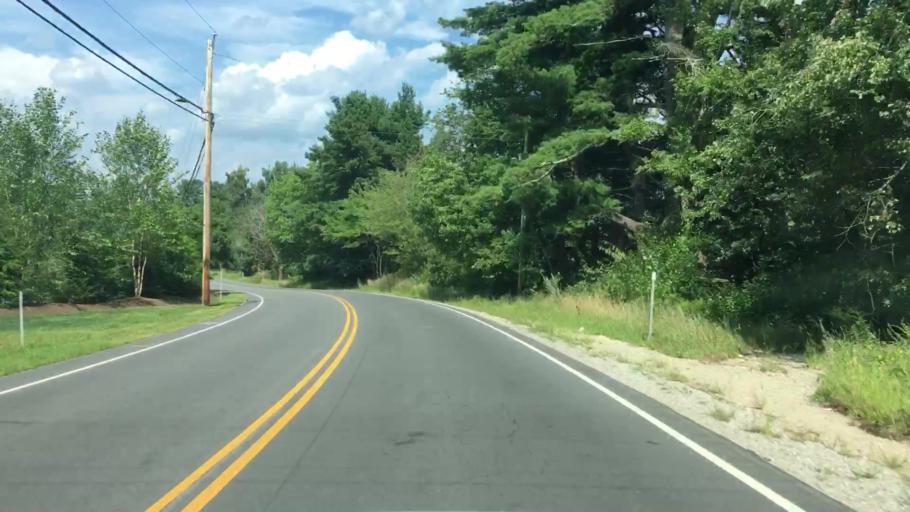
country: US
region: New Hampshire
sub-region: Rockingham County
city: Windham
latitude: 42.7981
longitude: -71.3527
